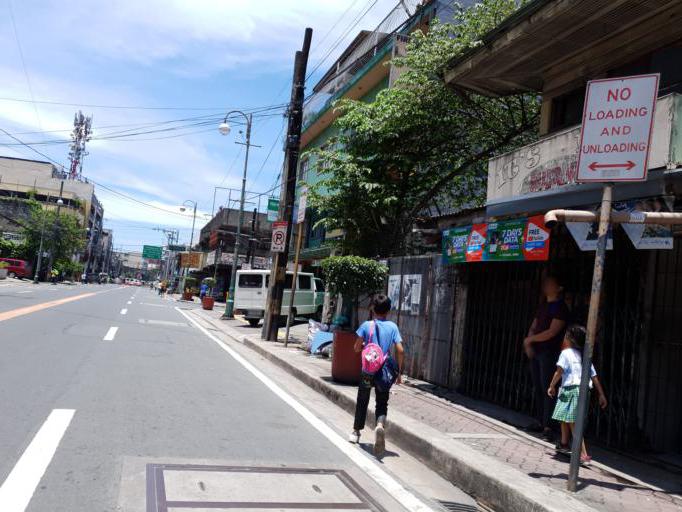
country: PH
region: Metro Manila
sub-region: Makati City
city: Makati City
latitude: 14.5715
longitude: 121.0172
